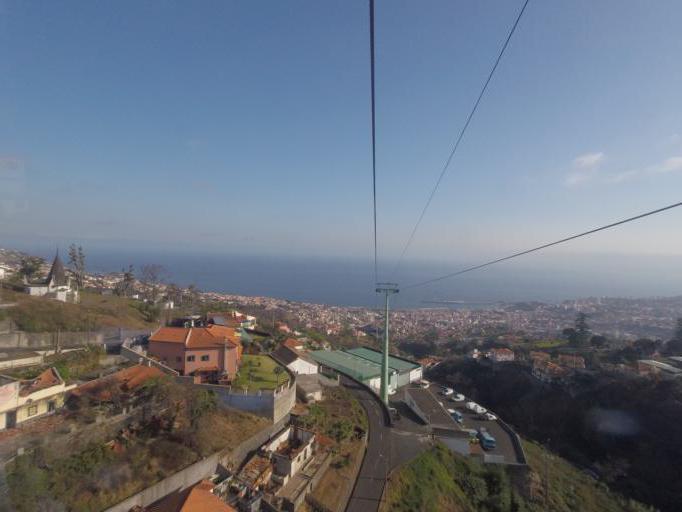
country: PT
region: Madeira
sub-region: Funchal
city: Nossa Senhora do Monte
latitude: 32.6708
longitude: -16.9005
